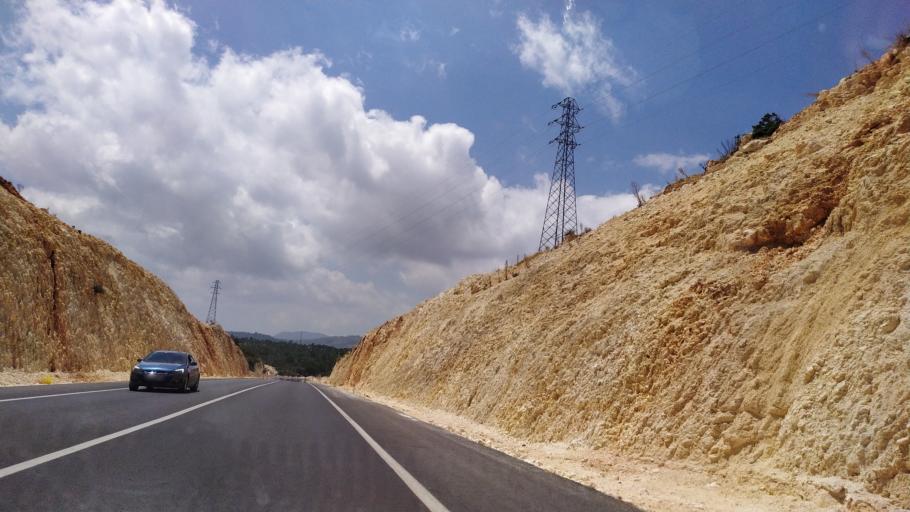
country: TR
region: Mersin
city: Gulnar
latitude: 36.2669
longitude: 33.3688
